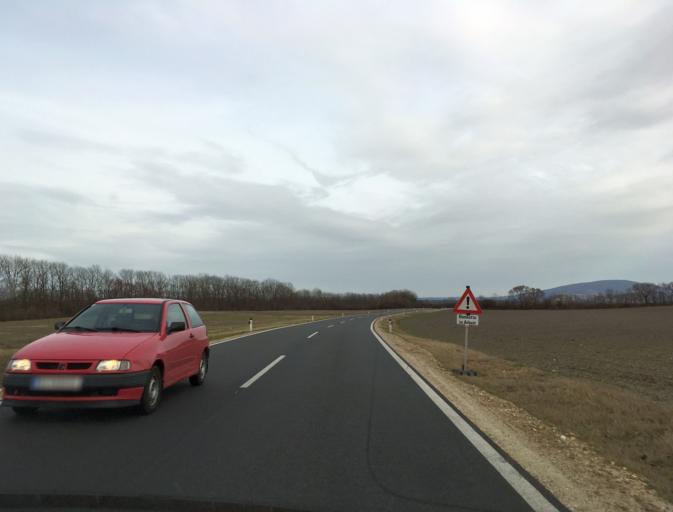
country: AT
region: Lower Austria
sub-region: Politischer Bezirk Ganserndorf
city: Lassee
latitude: 48.2226
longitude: 16.8719
